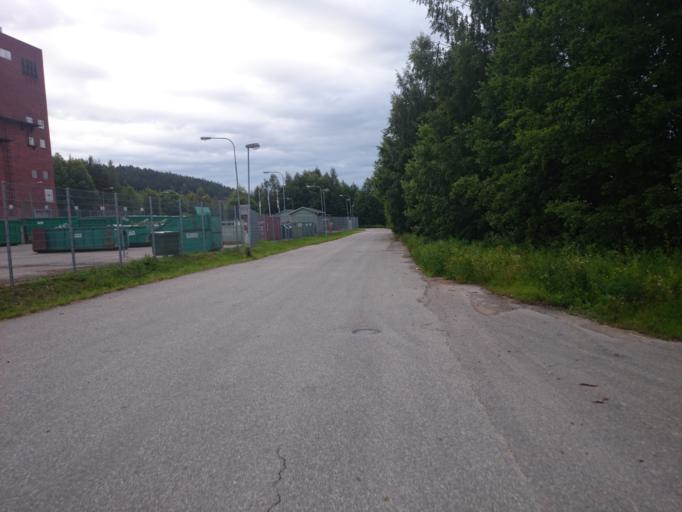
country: SE
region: Vaesternorrland
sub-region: Sundsvalls Kommun
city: Kvissleby
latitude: 62.3093
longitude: 17.3759
